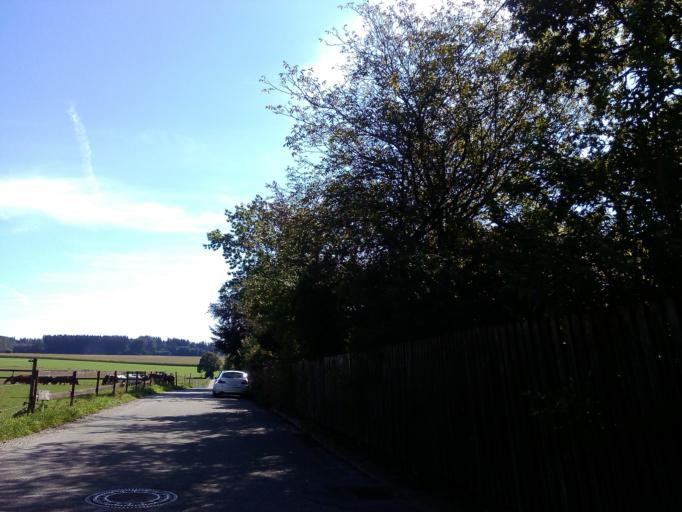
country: DE
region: Bavaria
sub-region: Upper Bavaria
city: Gauting
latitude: 48.0683
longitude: 11.3299
